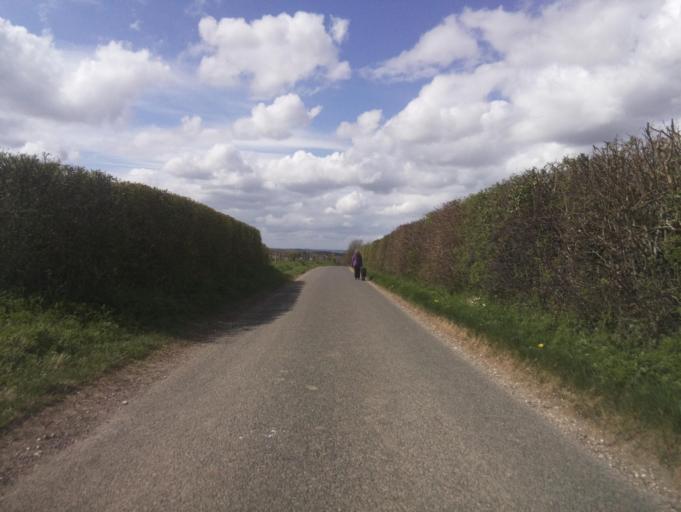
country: GB
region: England
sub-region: West Berkshire
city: Kintbury
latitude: 51.3690
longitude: -1.4791
